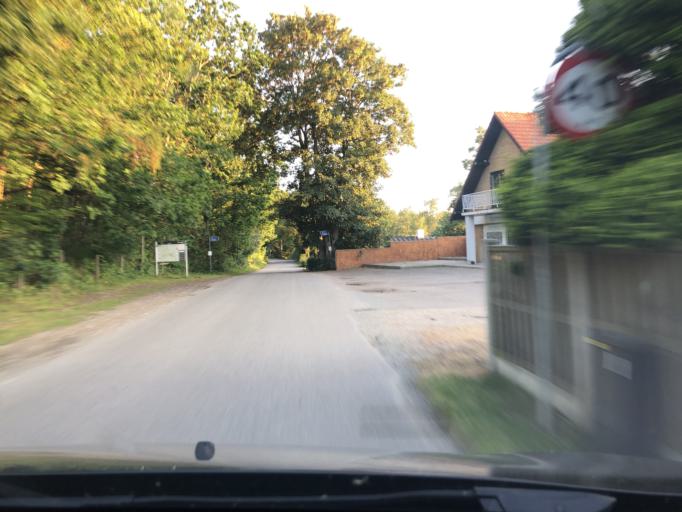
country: DK
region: South Denmark
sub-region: Vejle Kommune
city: Brejning
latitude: 55.6418
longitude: 9.7411
